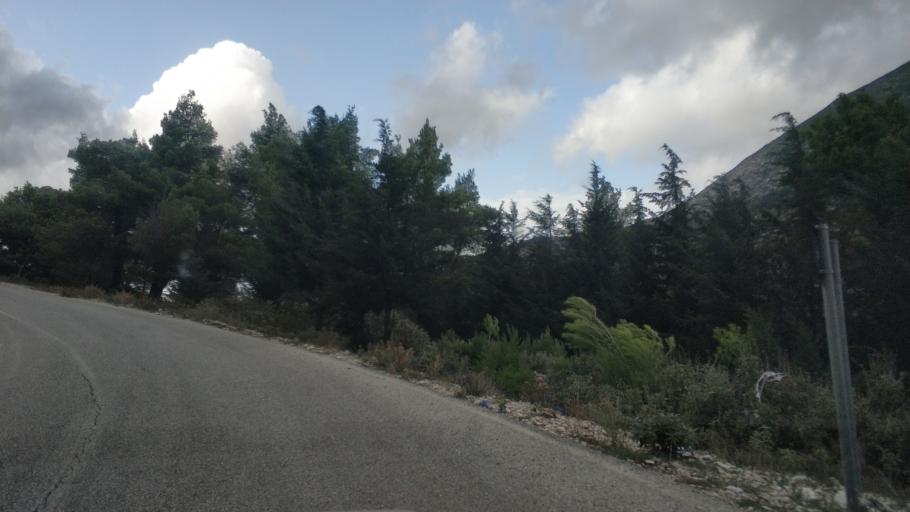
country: AL
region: Vlore
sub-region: Rrethi i Vlores
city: Orikum
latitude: 40.2507
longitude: 19.5418
